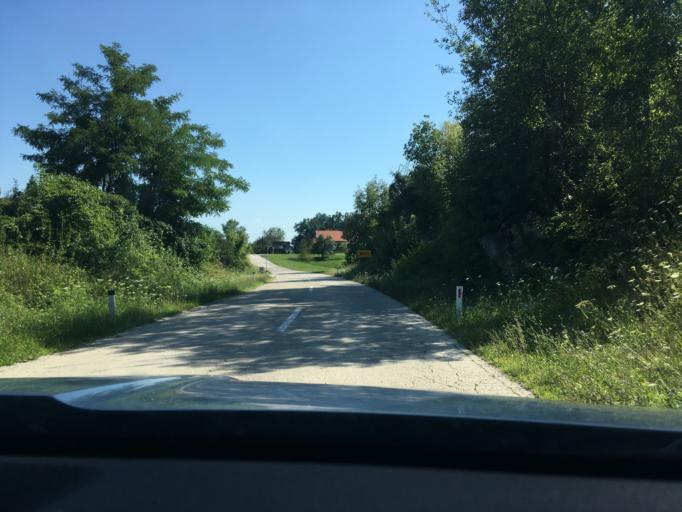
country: HR
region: Karlovacka
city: Ozalj
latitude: 45.4921
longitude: 15.3609
